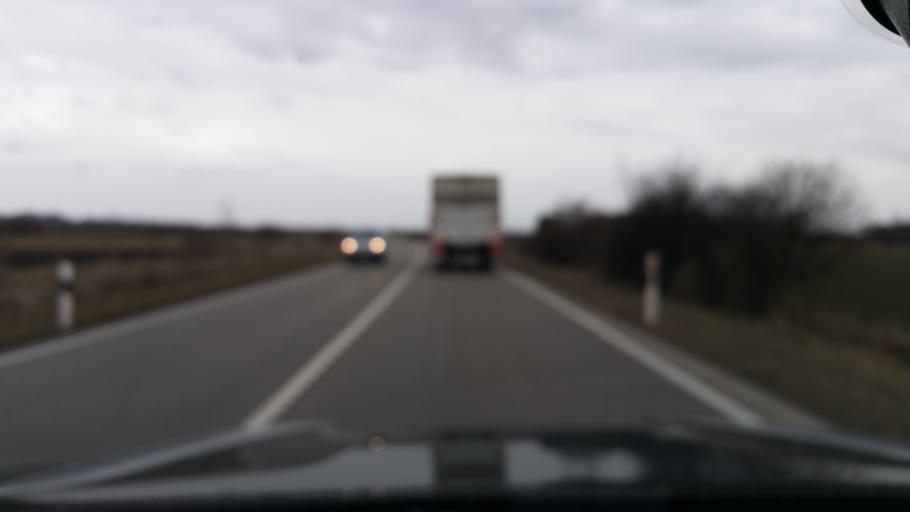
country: DE
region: Bavaria
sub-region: Upper Bavaria
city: Eitting
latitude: 48.3793
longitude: 11.8600
